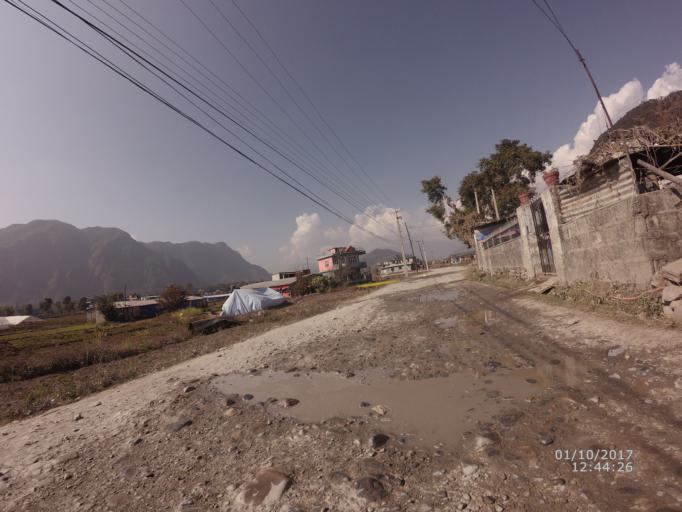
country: NP
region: Western Region
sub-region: Gandaki Zone
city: Pokhara
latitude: 28.2686
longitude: 83.9628
